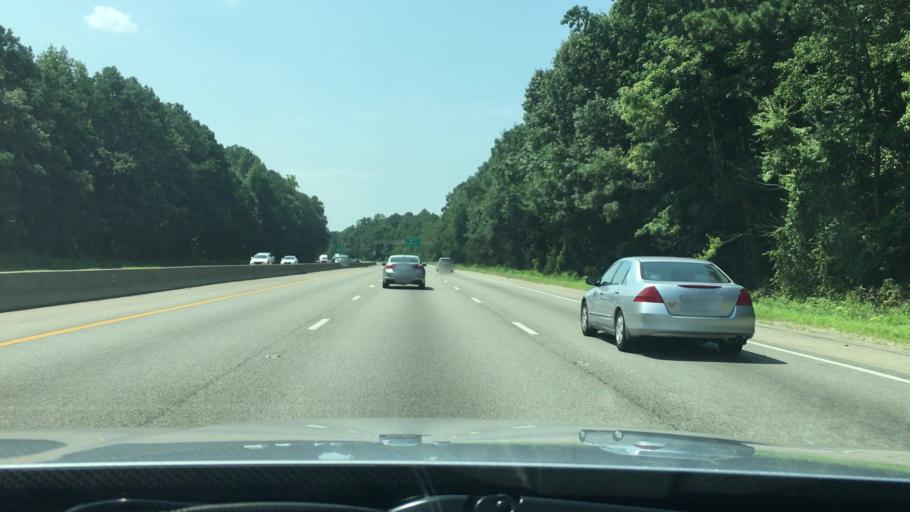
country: US
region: Virginia
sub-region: Chesterfield County
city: Chester
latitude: 37.3248
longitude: -77.4001
